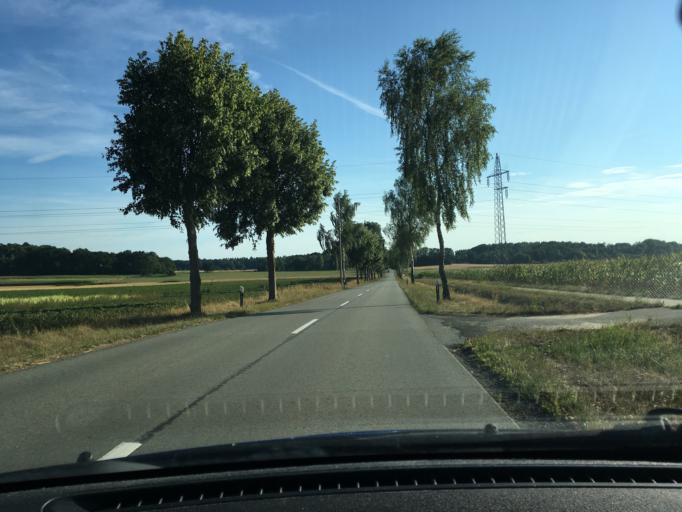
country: DE
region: Lower Saxony
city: Thomasburg
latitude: 53.1929
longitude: 10.6343
